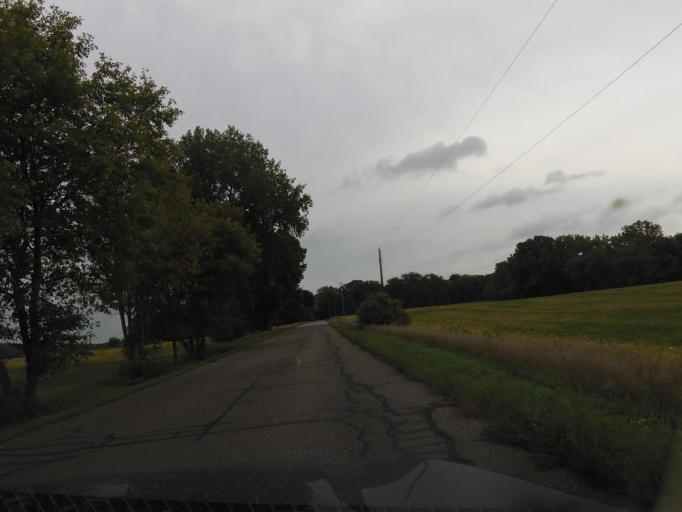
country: US
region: Minnesota
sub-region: Washington County
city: Afton
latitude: 44.8763
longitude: -92.8307
